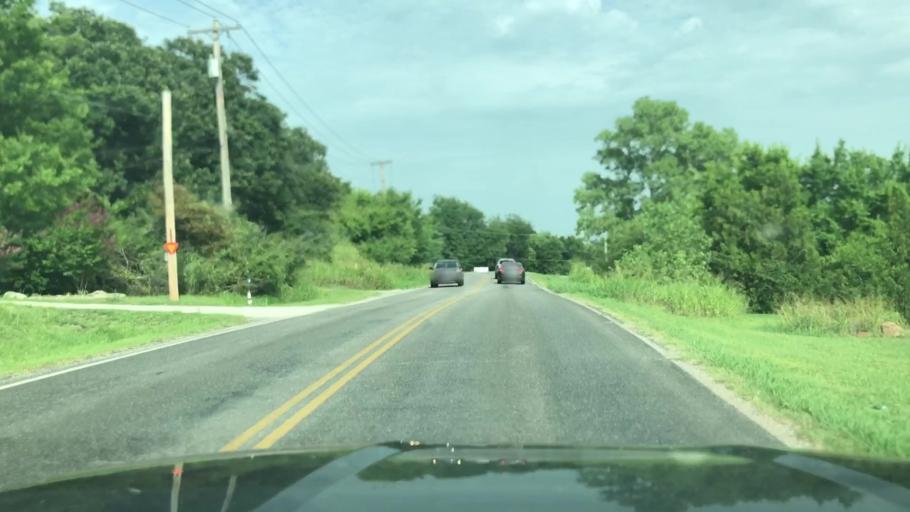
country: US
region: Oklahoma
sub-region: Tulsa County
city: Oakhurst
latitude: 36.0886
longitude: -96.0737
